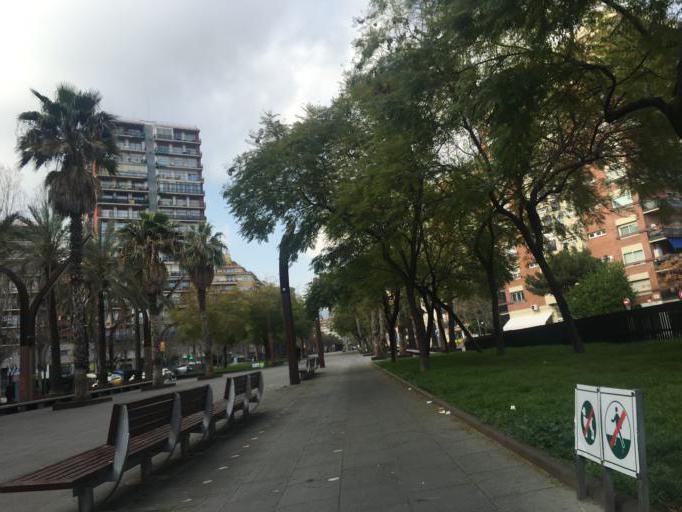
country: ES
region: Catalonia
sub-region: Provincia de Barcelona
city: les Corts
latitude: 41.3808
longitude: 2.1287
